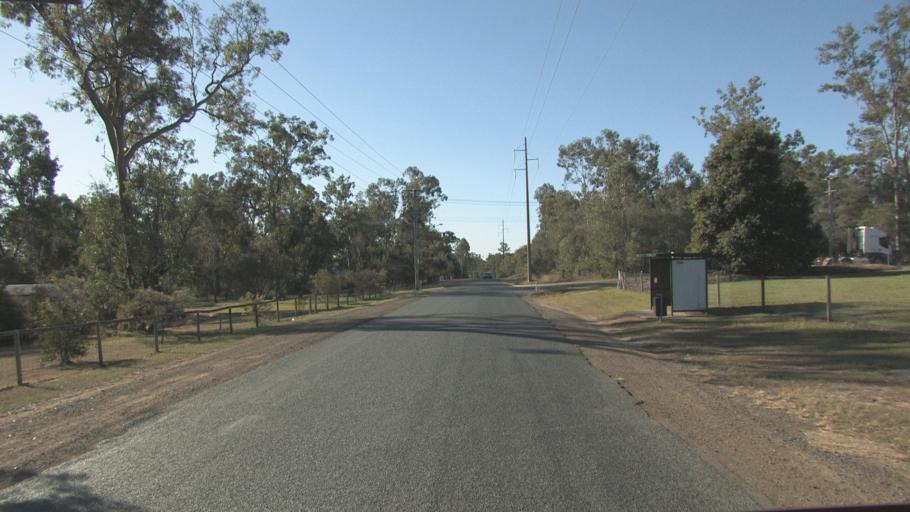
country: AU
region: Queensland
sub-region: Logan
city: North Maclean
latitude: -27.7984
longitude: 153.0416
